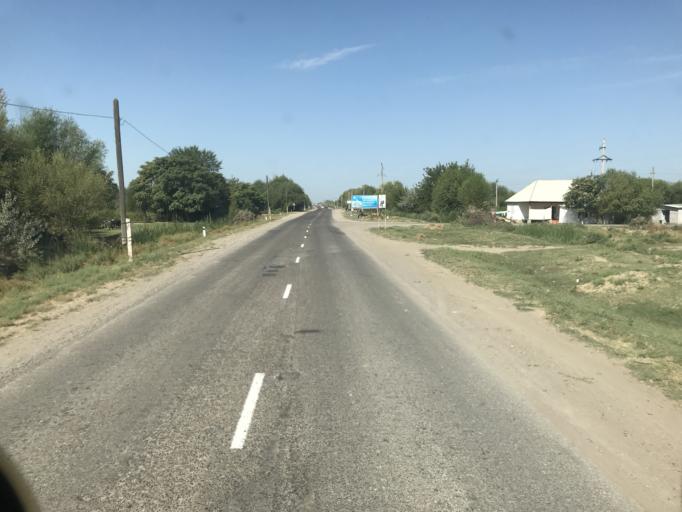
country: KZ
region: Ongtustik Qazaqstan
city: Myrzakent
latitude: 40.6851
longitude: 68.5925
